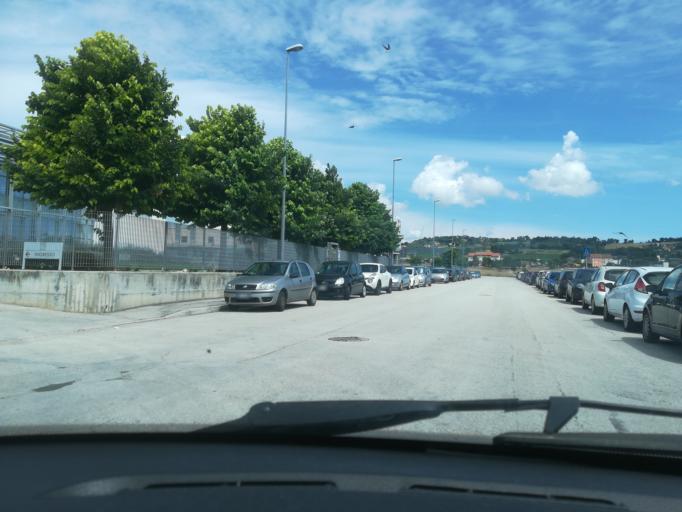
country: IT
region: The Marches
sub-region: Provincia di Macerata
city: Santa Maria Apparente
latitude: 43.2875
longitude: 13.6798
